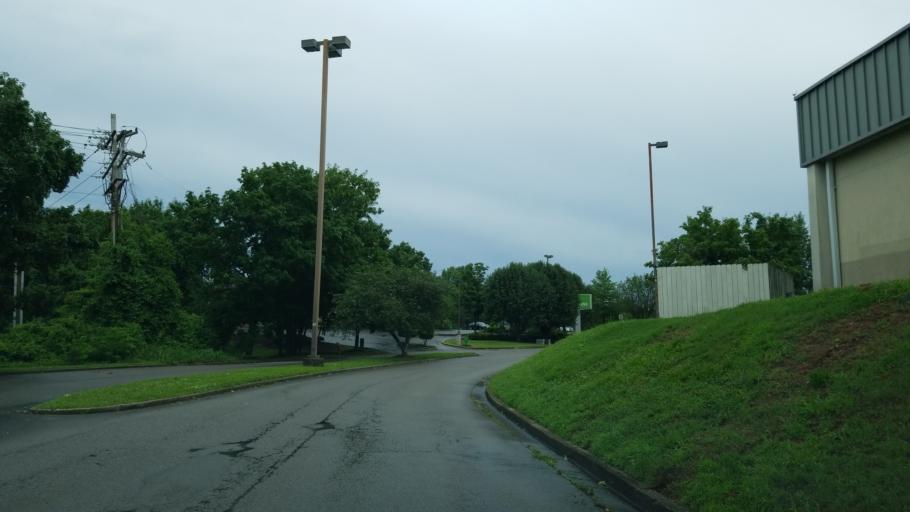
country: US
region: Tennessee
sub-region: Rutherford County
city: La Vergne
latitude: 36.0491
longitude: -86.6593
